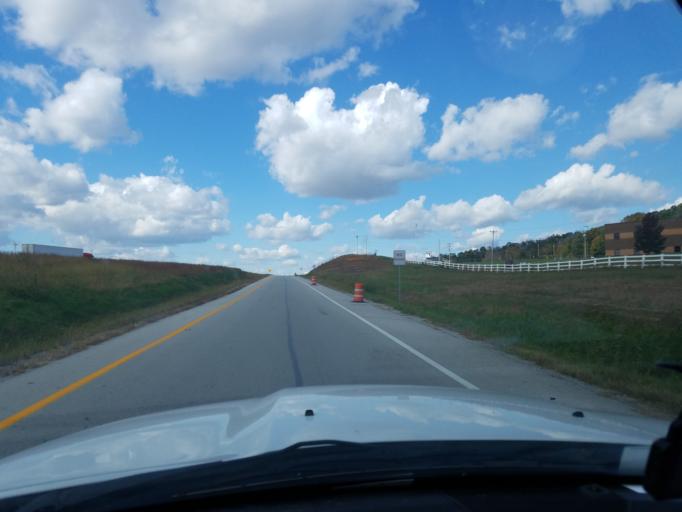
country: US
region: Kentucky
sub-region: Butler County
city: Morgantown
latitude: 37.2040
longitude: -86.7012
